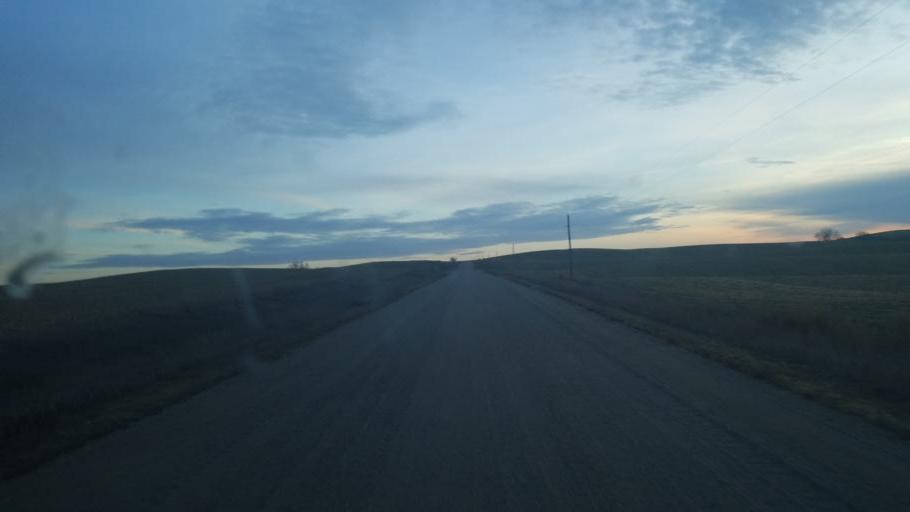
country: US
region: Nebraska
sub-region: Knox County
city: Center
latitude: 42.6840
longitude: -97.7599
